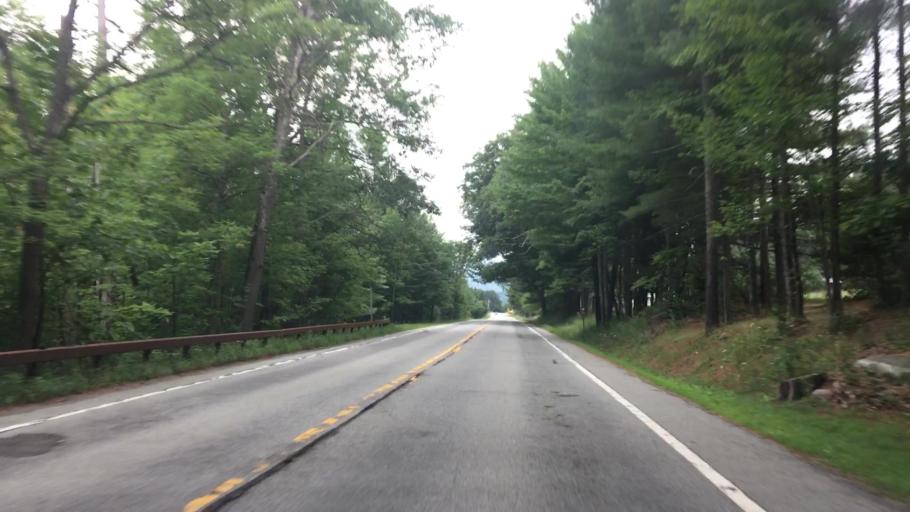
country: US
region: New York
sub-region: Essex County
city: Elizabethtown
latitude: 44.3952
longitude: -73.7093
